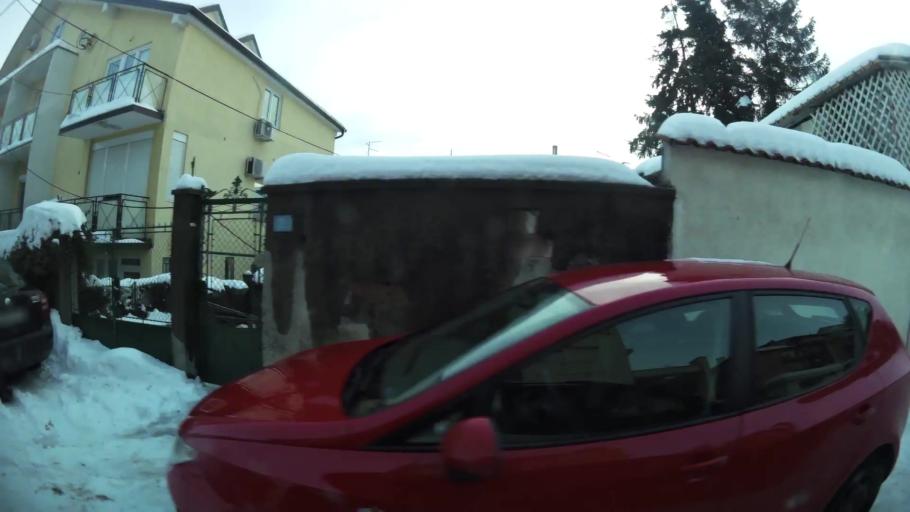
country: RS
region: Central Serbia
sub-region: Belgrade
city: Palilula
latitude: 44.7948
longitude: 20.5143
